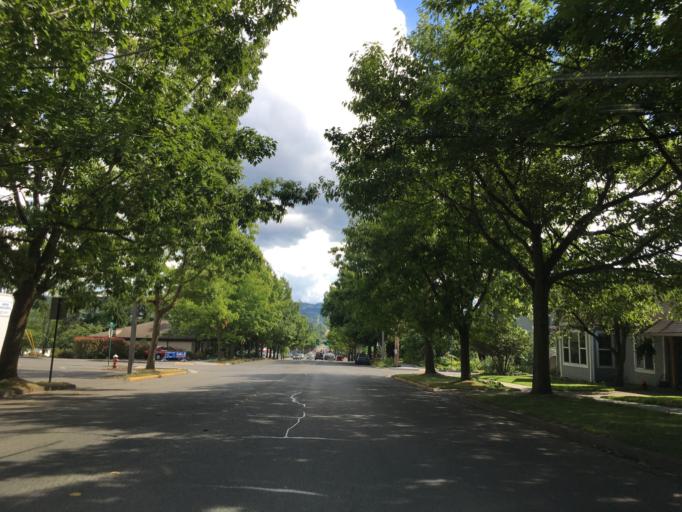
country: US
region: Washington
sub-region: Whatcom County
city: Bellingham
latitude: 48.7648
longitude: -122.4650
